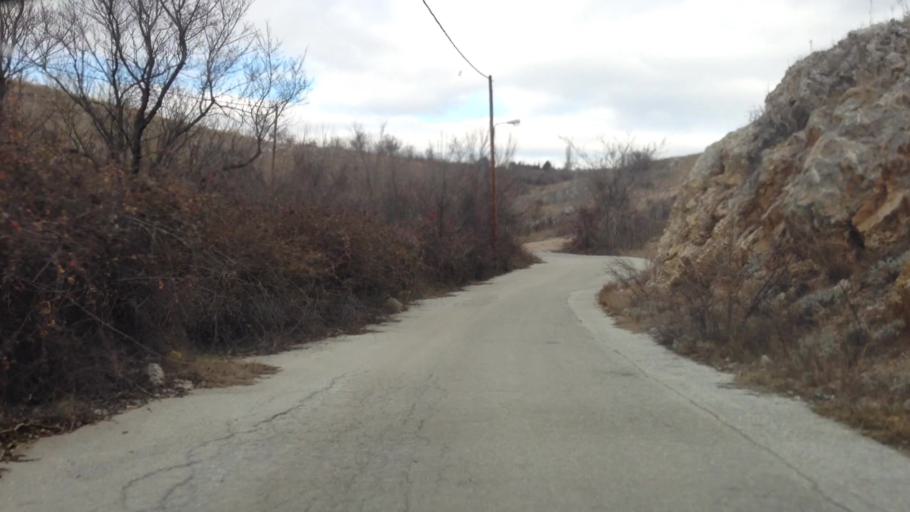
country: GR
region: West Macedonia
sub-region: Nomos Kozanis
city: Kozani
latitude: 40.2959
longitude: 21.7704
